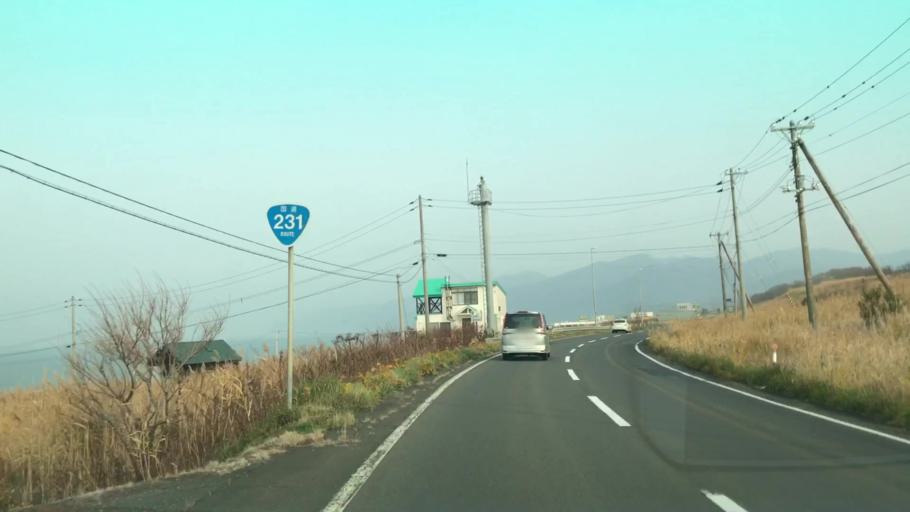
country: JP
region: Hokkaido
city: Ishikari
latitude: 43.3710
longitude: 141.4266
